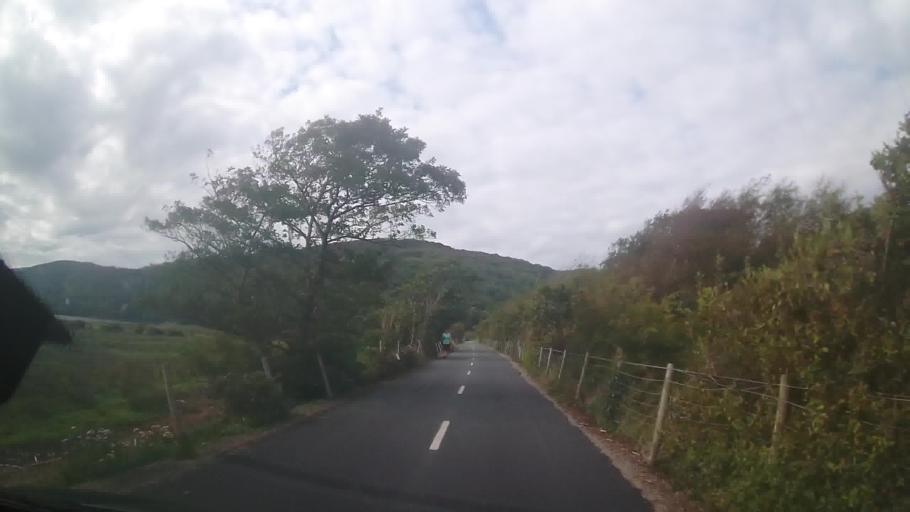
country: GB
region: Wales
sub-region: Gwynedd
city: Dolgellau
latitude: 52.7503
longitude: -3.9388
